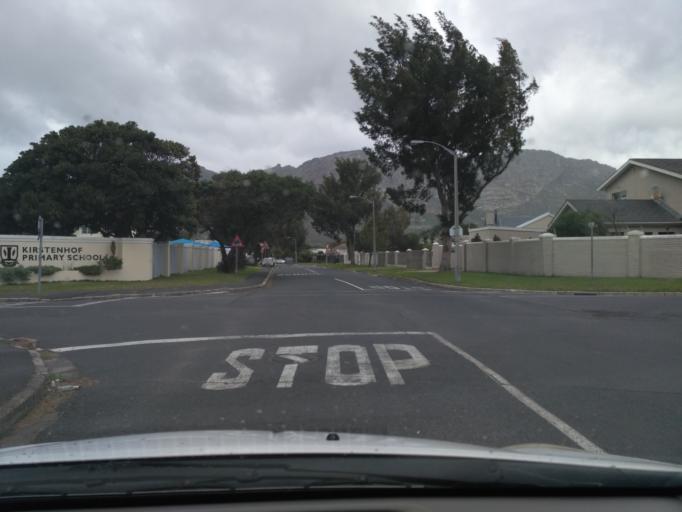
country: ZA
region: Western Cape
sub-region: City of Cape Town
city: Bergvliet
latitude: -34.0684
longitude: 18.4541
